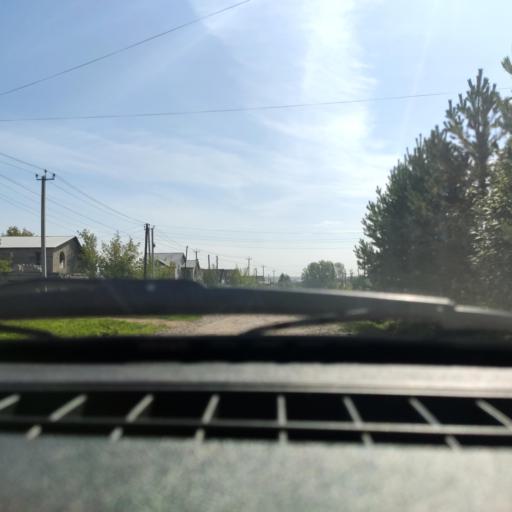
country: RU
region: Bashkortostan
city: Iglino
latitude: 54.8499
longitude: 56.4258
